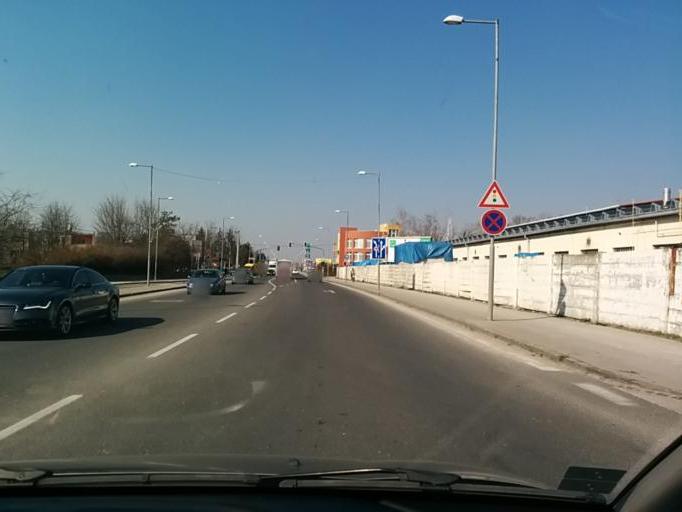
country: SK
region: Trnavsky
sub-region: Okres Galanta
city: Galanta
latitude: 48.1961
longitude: 17.7340
